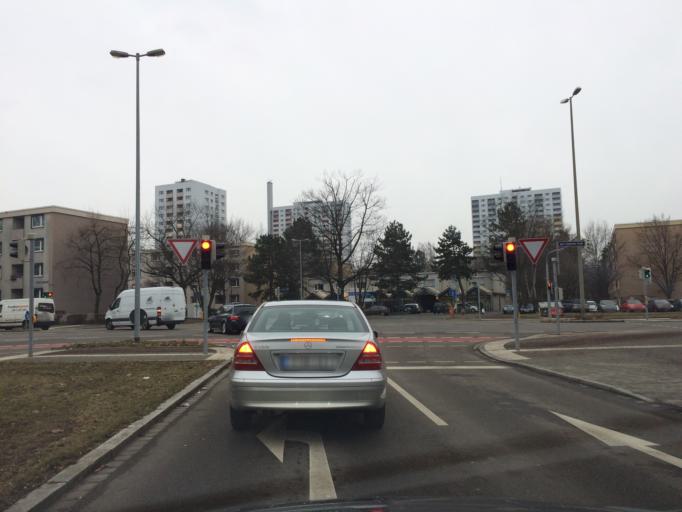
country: DE
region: Bavaria
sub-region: Regierungsbezirk Mittelfranken
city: Nuernberg
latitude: 49.4128
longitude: 11.1156
